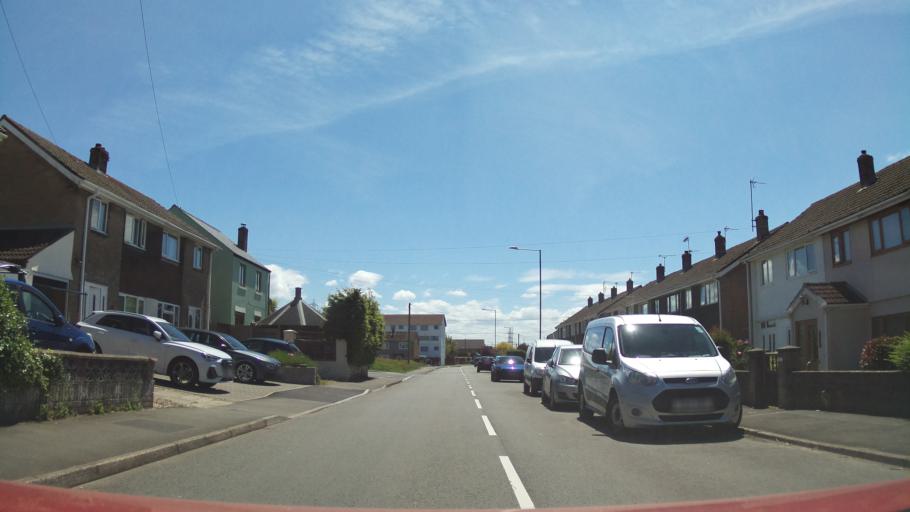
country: GB
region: Wales
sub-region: Monmouthshire
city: Caldicot
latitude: 51.5886
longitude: -2.7641
